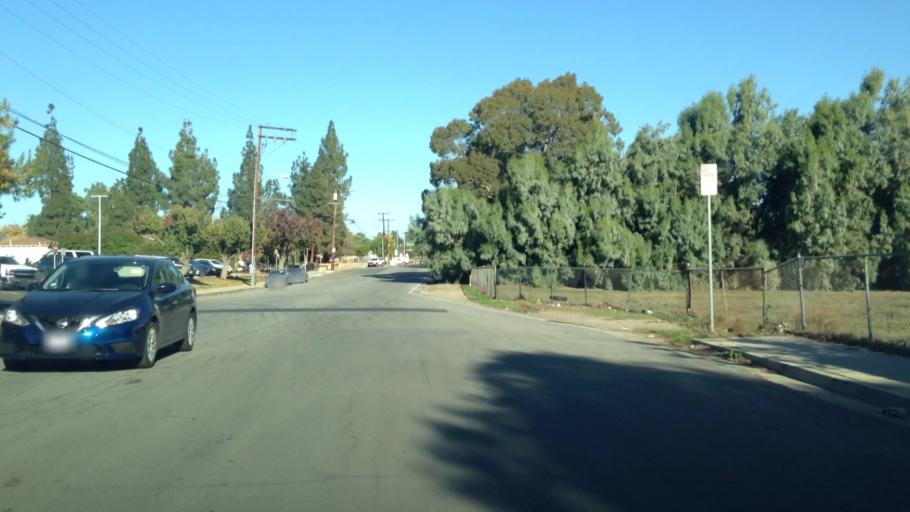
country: US
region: California
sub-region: Riverside County
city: Pedley
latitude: 33.9311
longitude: -117.4792
